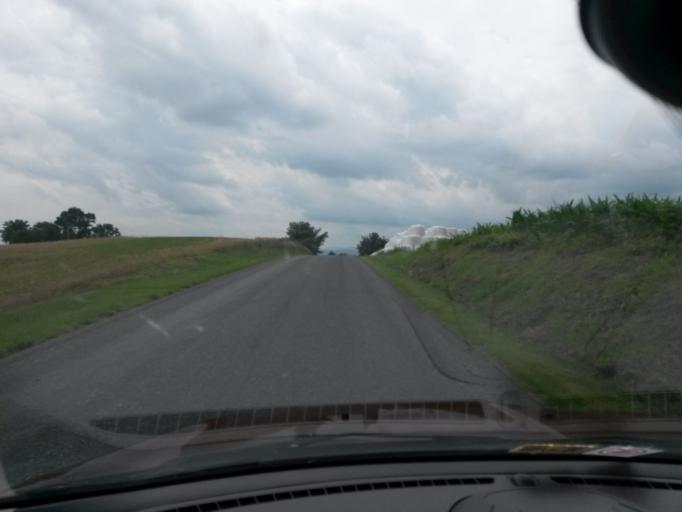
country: US
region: Virginia
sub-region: Rockingham County
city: Dayton
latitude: 38.4482
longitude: -78.9626
